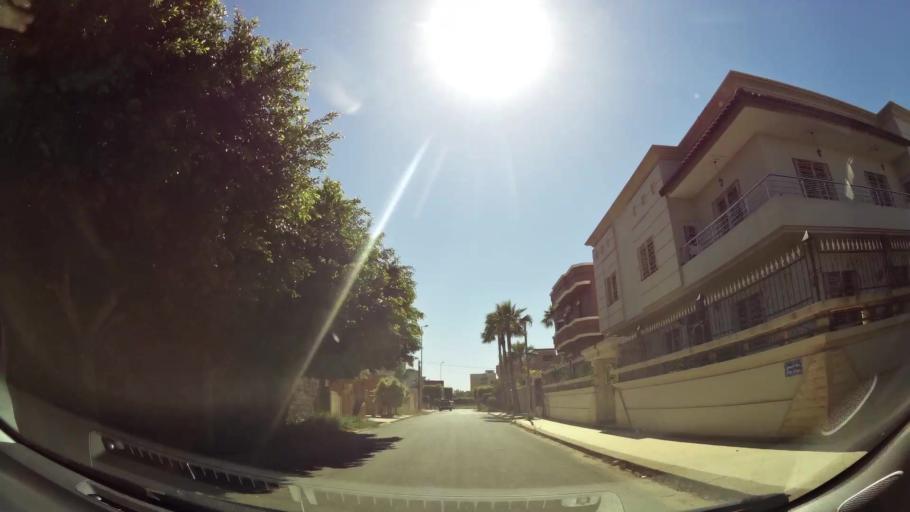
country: MA
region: Oriental
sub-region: Berkane-Taourirt
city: Berkane
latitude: 34.9447
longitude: -2.3265
